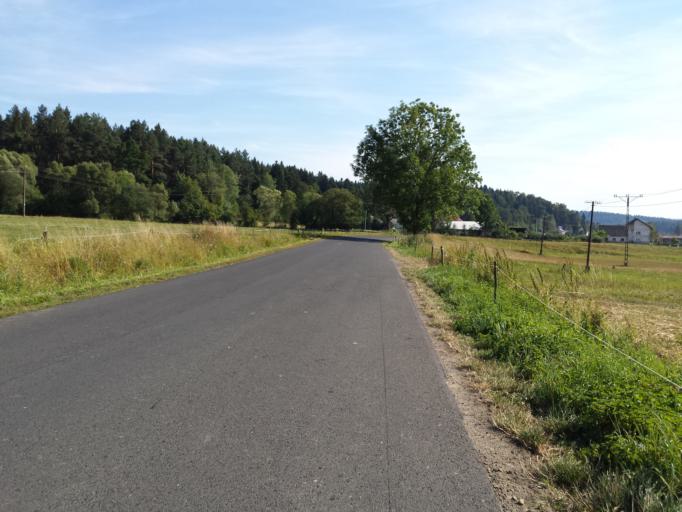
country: PL
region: Subcarpathian Voivodeship
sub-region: Powiat leski
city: Olszanica
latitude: 49.4961
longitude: 22.4499
